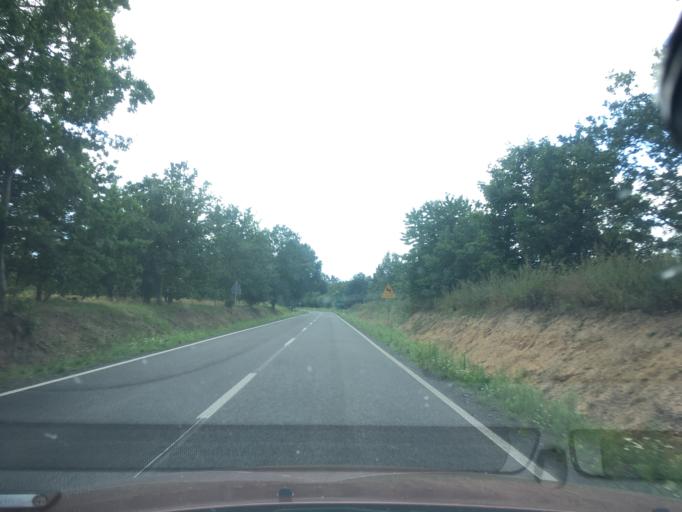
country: PL
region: Lower Silesian Voivodeship
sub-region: Powiat zgorzelecki
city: Zgorzelec
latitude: 51.1926
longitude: 15.0115
